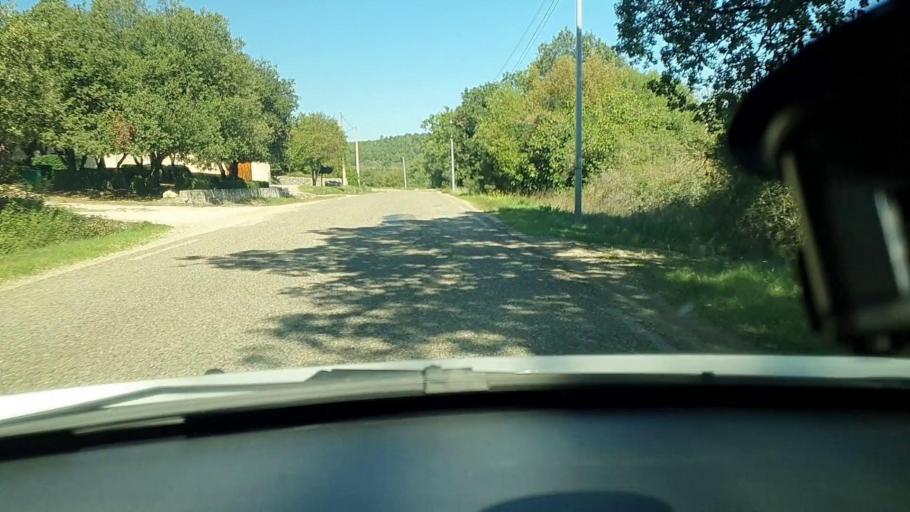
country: FR
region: Languedoc-Roussillon
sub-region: Departement du Gard
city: Goudargues
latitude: 44.1564
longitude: 4.4584
